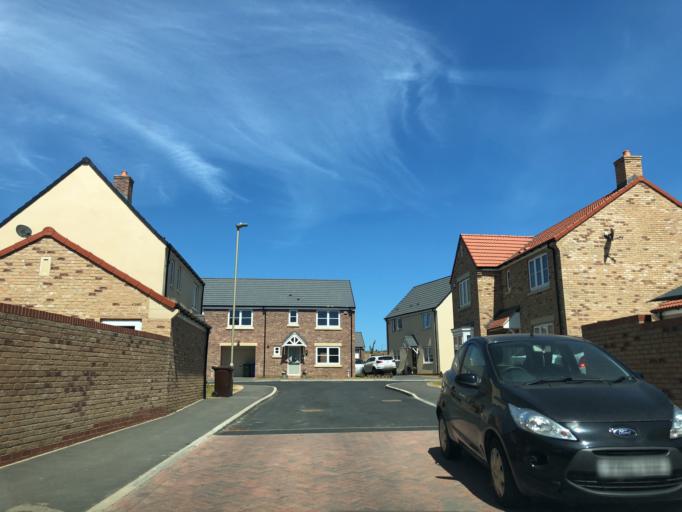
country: GB
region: England
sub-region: North Yorkshire
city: Scarborough
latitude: 54.2465
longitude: -0.3864
